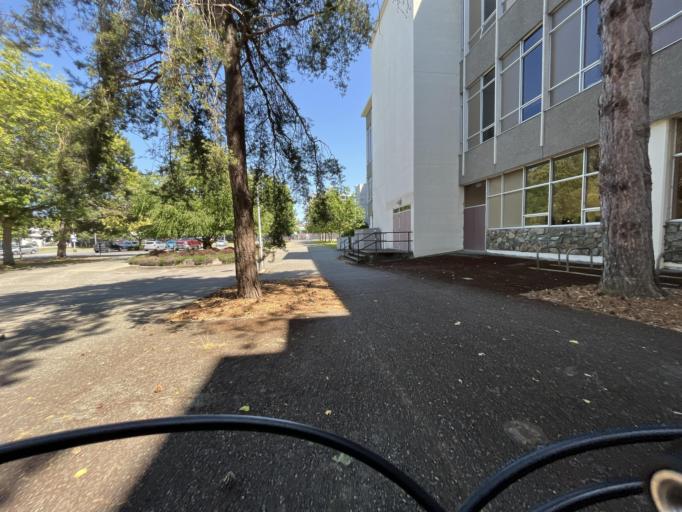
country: CA
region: British Columbia
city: Oak Bay
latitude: 48.4639
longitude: -123.3097
